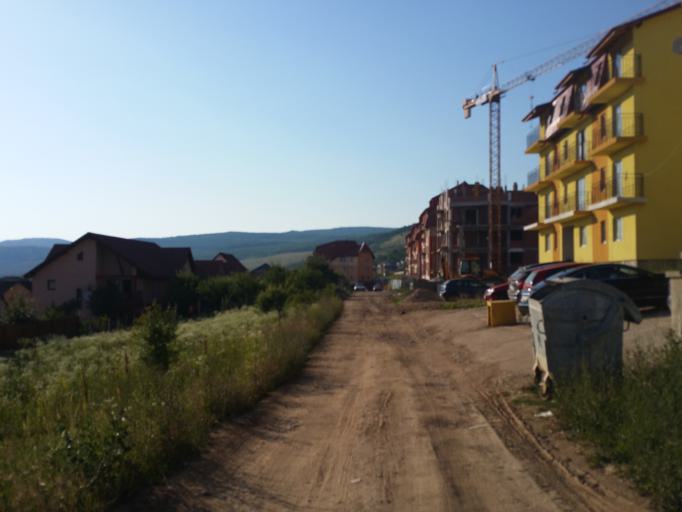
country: RO
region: Cluj
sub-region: Comuna Baciu
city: Baciu
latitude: 46.7897
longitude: 23.5319
